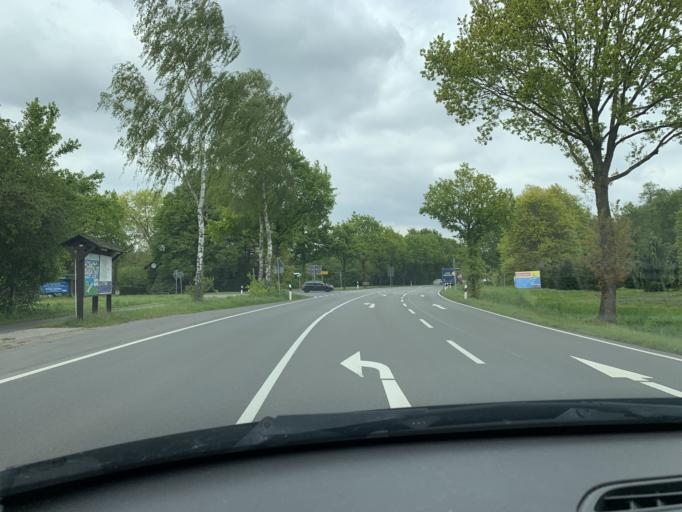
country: DE
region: Lower Saxony
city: Bad Zwischenahn
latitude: 53.2054
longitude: 8.0401
